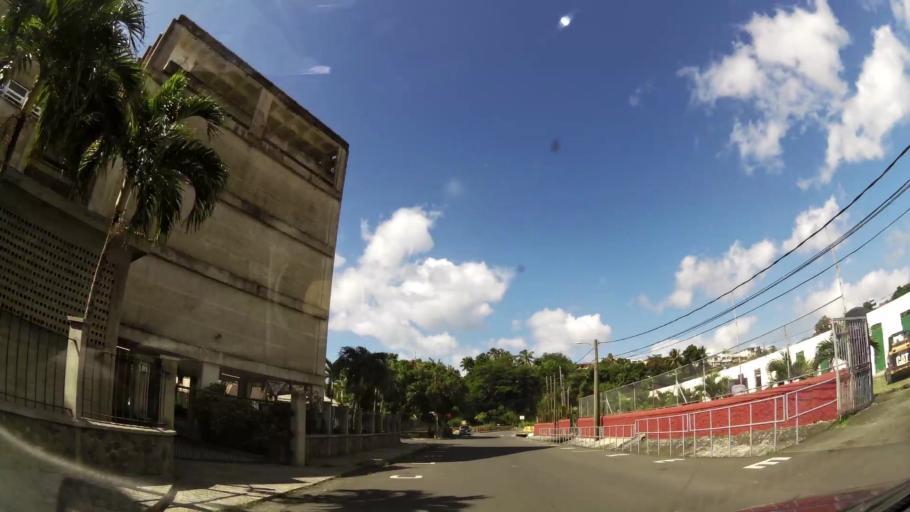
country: DM
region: Saint George
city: Roseau
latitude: 15.3015
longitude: -61.3857
